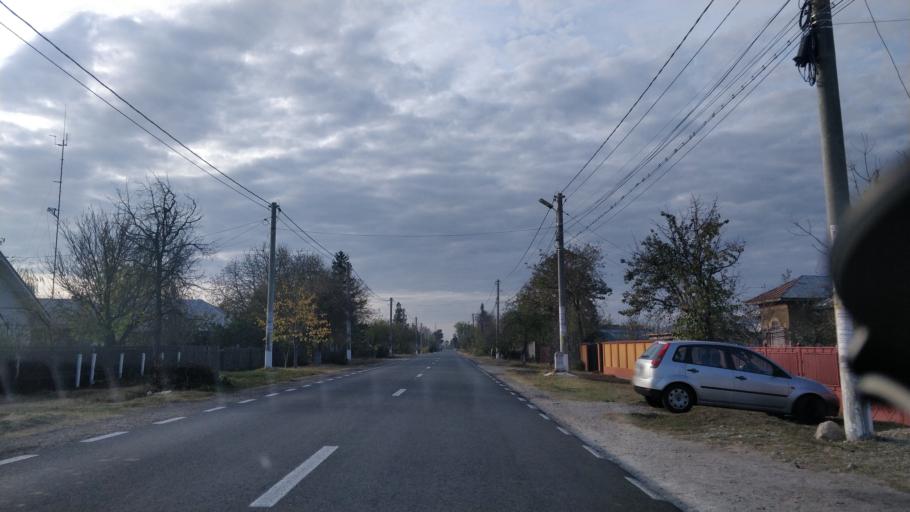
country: RO
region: Giurgiu
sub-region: Comuna Clejani
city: Clejani
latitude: 44.3411
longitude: 25.6797
